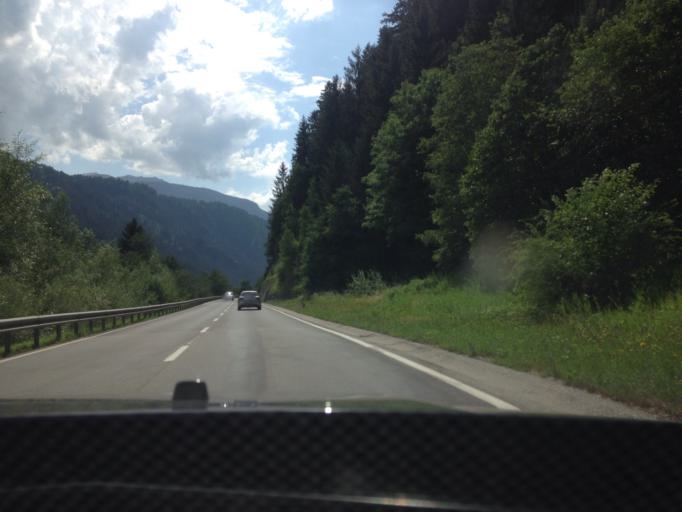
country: CH
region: Grisons
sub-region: Surselva District
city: Breil
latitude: 46.7692
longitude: 9.1131
